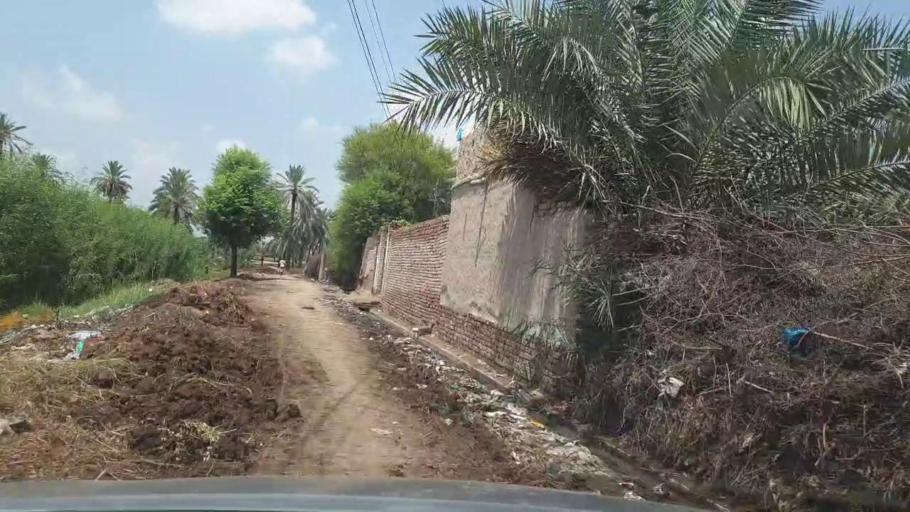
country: PK
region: Sindh
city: Pir jo Goth
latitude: 27.6120
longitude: 68.6041
